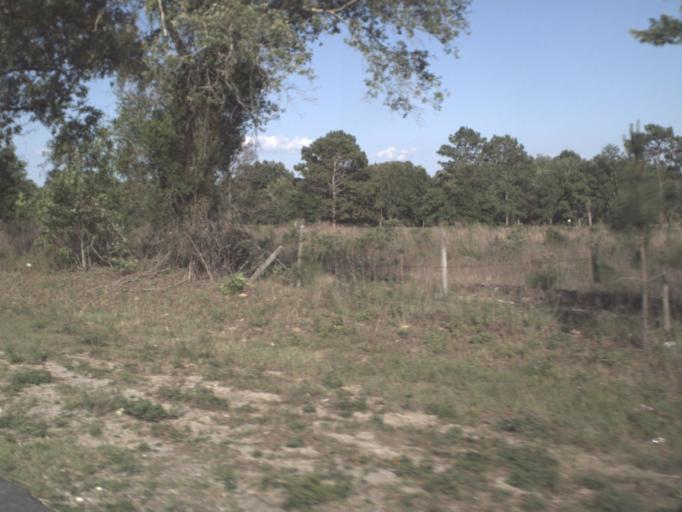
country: US
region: Florida
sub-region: Marion County
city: Dunnellon
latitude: 29.1226
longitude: -82.4294
